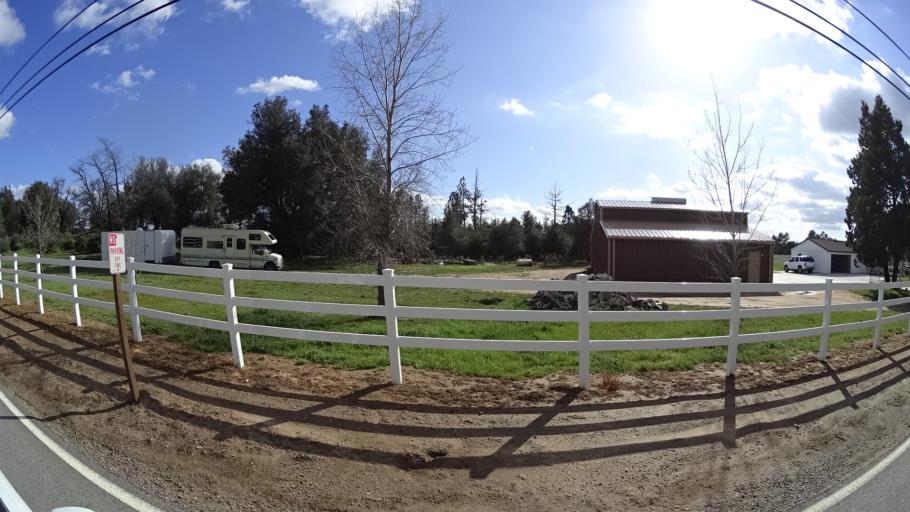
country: US
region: California
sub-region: San Diego County
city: Julian
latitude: 33.0985
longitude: -116.6479
